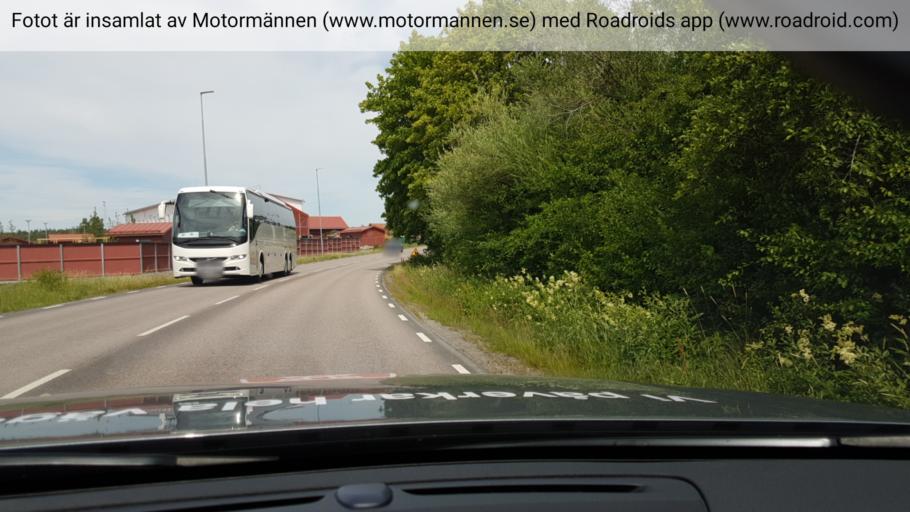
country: SE
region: Vaestmanland
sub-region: Vasteras
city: Vasteras
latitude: 59.6435
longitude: 16.5259
